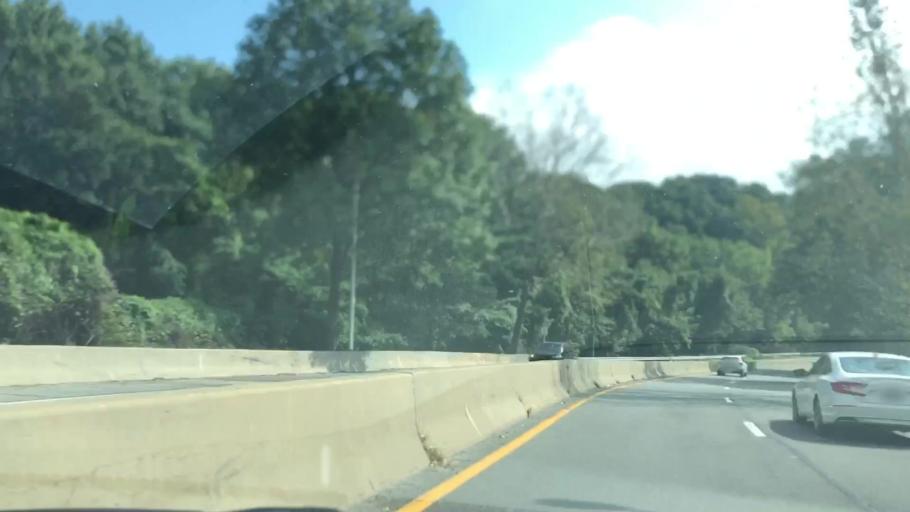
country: US
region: New York
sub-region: Westchester County
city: Yonkers
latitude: 40.9001
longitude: -73.8863
